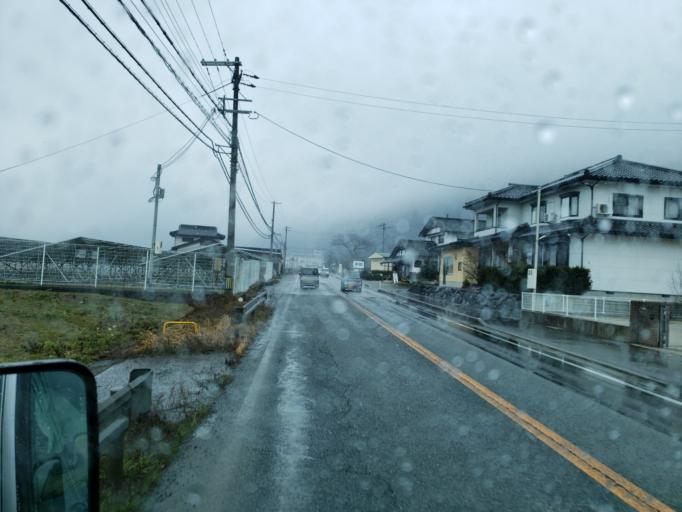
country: JP
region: Hyogo
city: Toyooka
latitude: 35.3863
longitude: 134.6931
